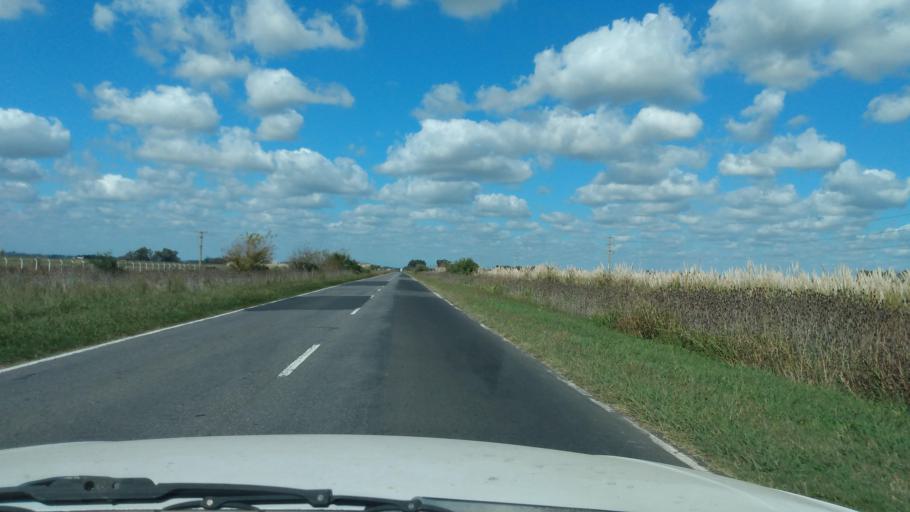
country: AR
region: Buenos Aires
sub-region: Partido de Navarro
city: Navarro
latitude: -34.8910
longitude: -59.3375
